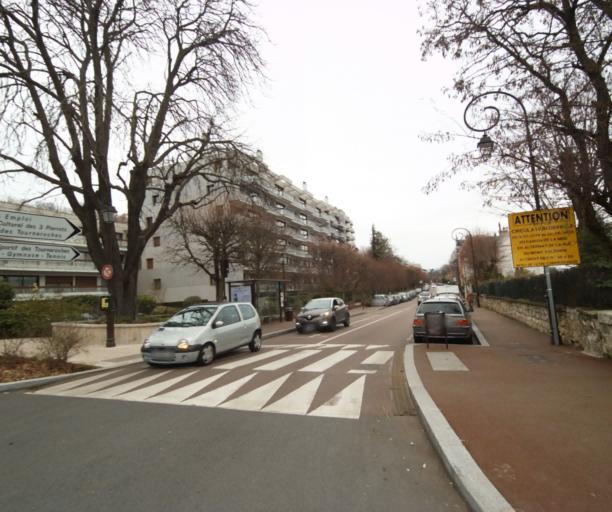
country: FR
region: Ile-de-France
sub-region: Departement des Hauts-de-Seine
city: Saint-Cloud
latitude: 48.8507
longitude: 2.2171
